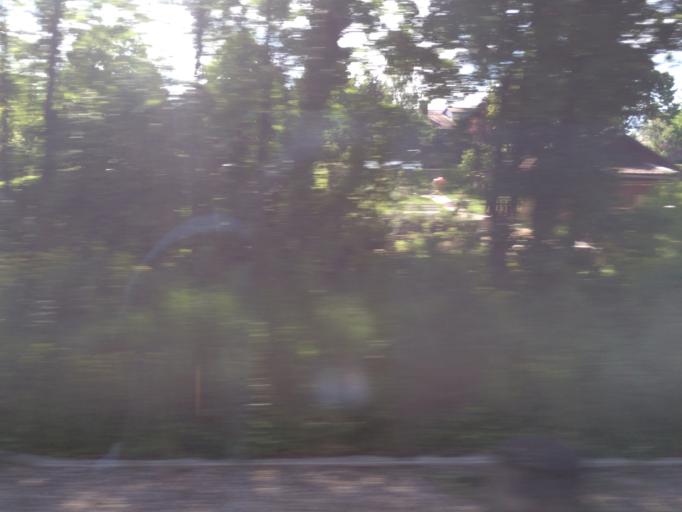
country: DE
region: Bavaria
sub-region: Regierungsbezirk Unterfranken
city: Kitzingen
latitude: 49.7448
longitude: 10.1583
